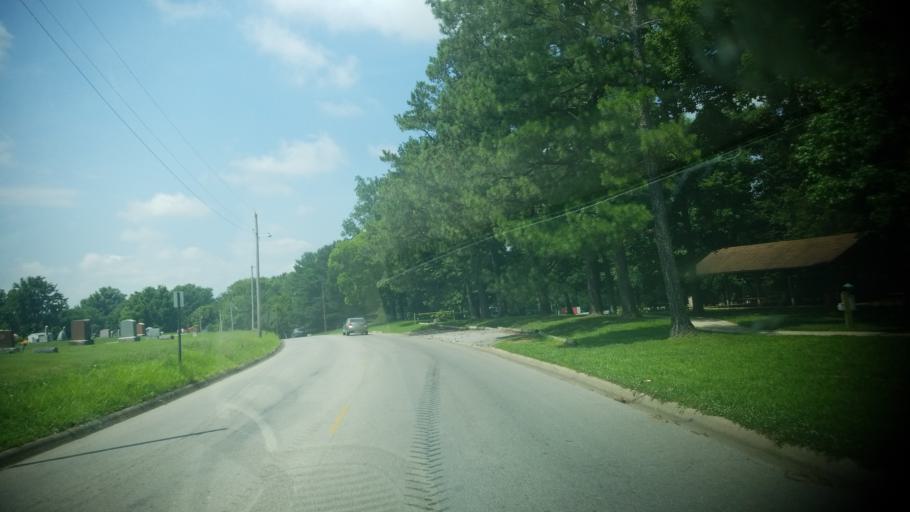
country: US
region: Illinois
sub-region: Wayne County
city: Fairfield
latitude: 38.3839
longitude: -88.3514
